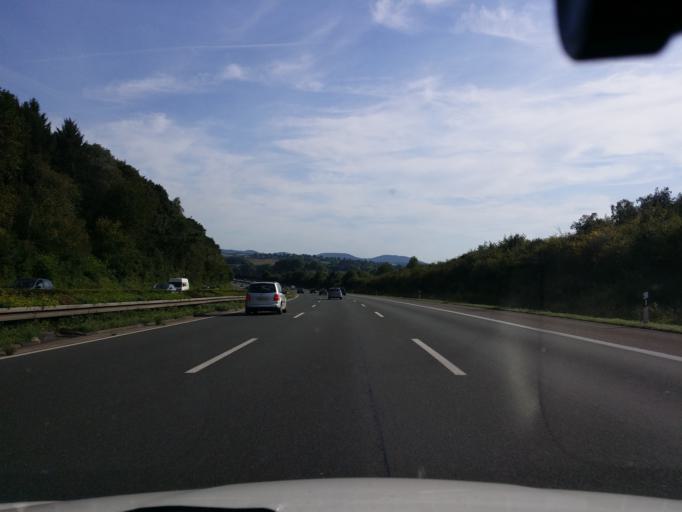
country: DE
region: North Rhine-Westphalia
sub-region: Regierungsbezirk Koln
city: Stossdorf
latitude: 50.7618
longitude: 7.2287
